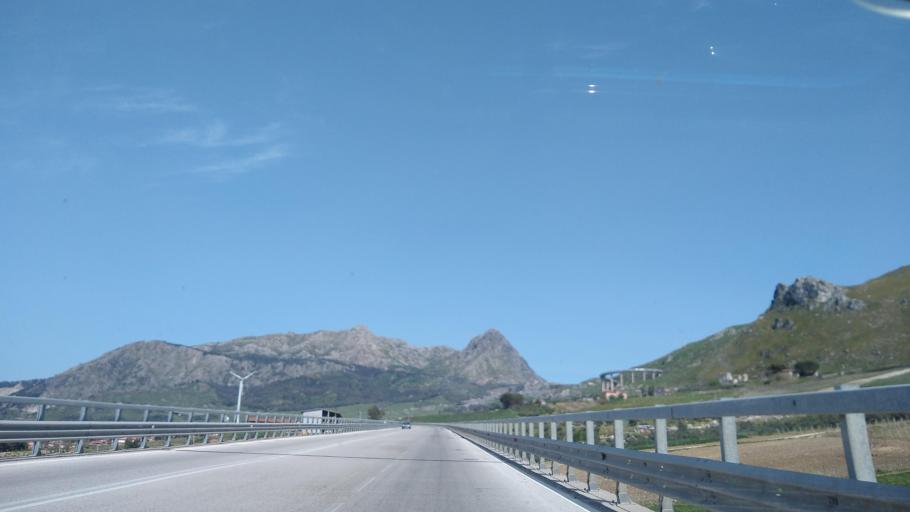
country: IT
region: Sicily
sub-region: Palermo
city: San Giuseppe Jato
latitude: 37.9756
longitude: 13.2129
